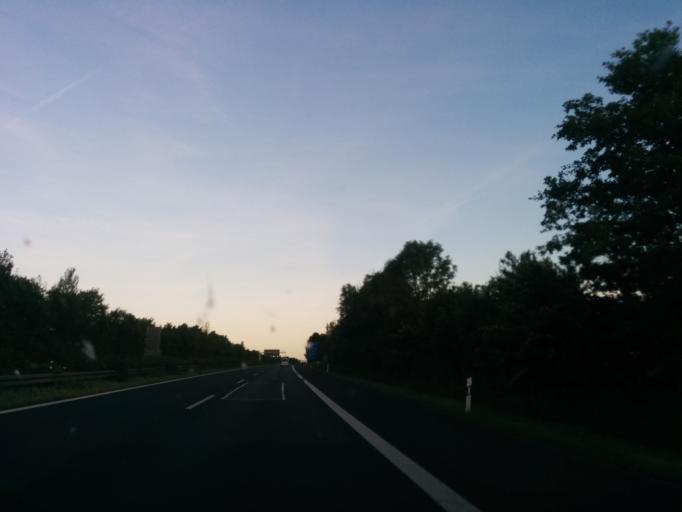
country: DE
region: Bavaria
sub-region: Regierungsbezirk Unterfranken
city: Biebelried
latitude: 49.7680
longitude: 10.1008
